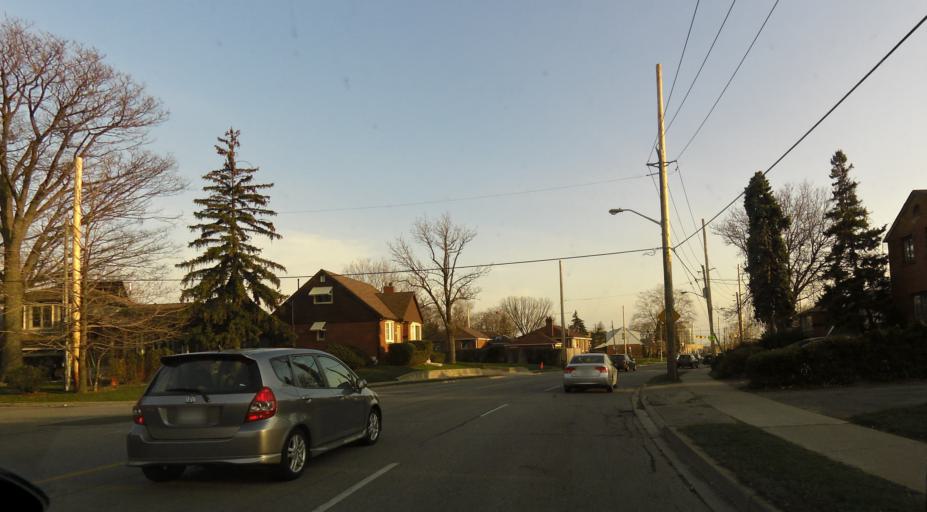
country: CA
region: Ontario
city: Etobicoke
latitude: 43.6364
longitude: -79.5565
